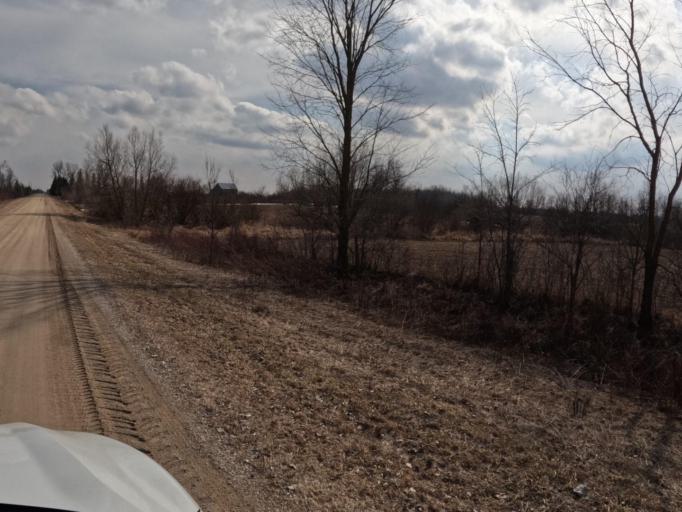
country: CA
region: Ontario
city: Shelburne
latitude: 43.9376
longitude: -80.3101
